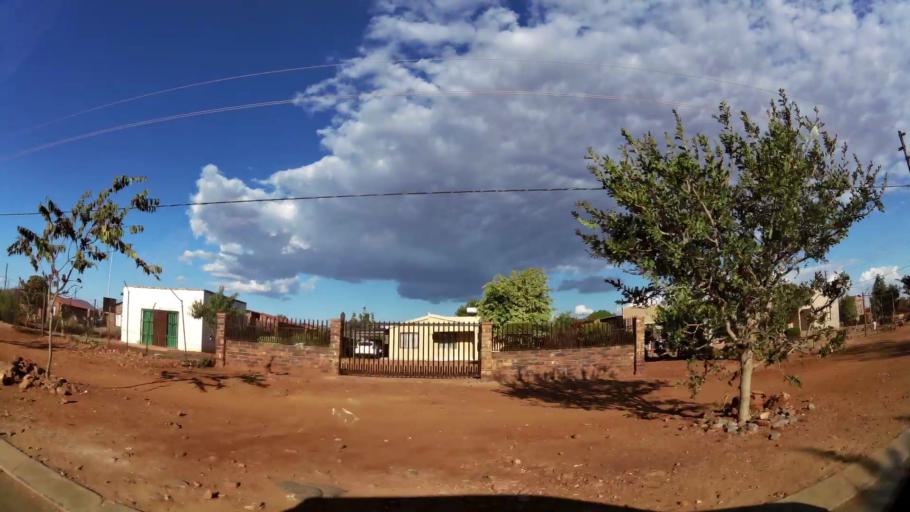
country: ZA
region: Limpopo
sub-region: Waterberg District Municipality
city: Mokopane
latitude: -24.1941
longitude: 28.9844
